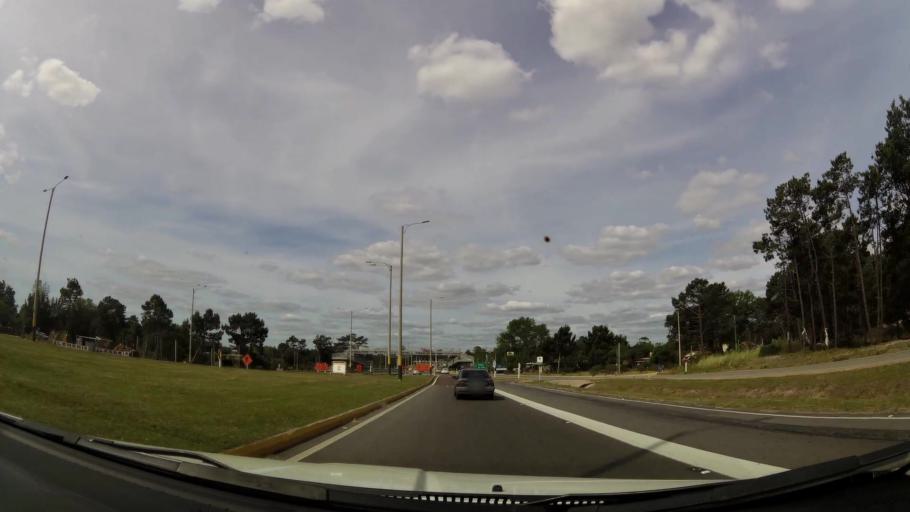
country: UY
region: Canelones
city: Empalme Olmos
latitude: -34.7888
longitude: -55.8940
